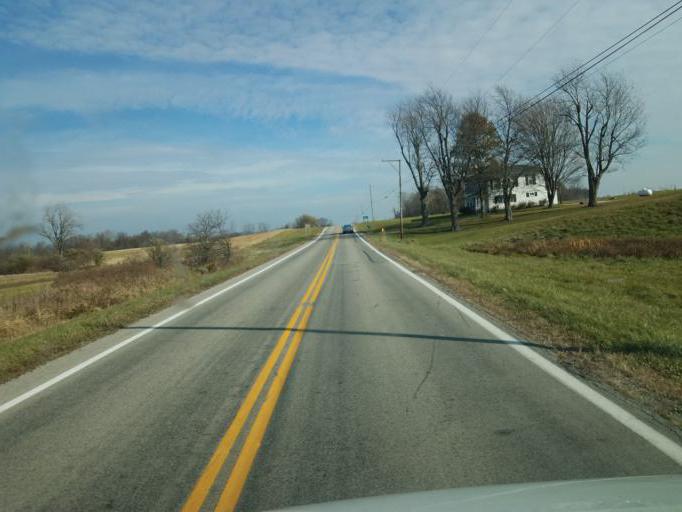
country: US
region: Ohio
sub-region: Hardin County
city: Forest
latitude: 40.7016
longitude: -83.4595
